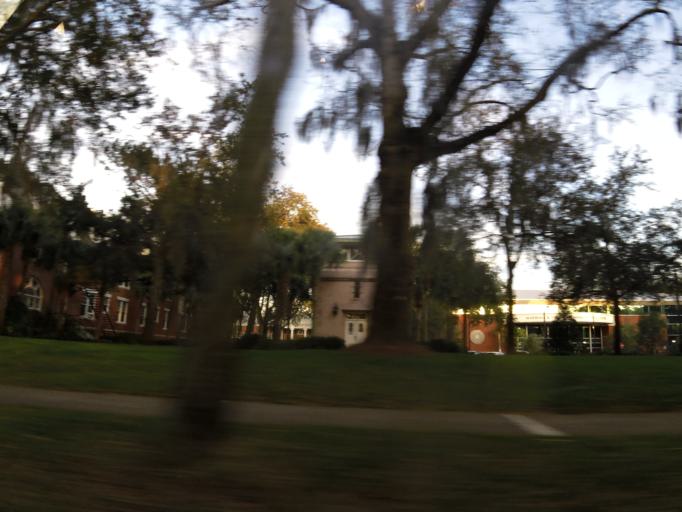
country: US
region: Florida
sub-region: Volusia County
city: DeLand
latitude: 29.0361
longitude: -81.3036
